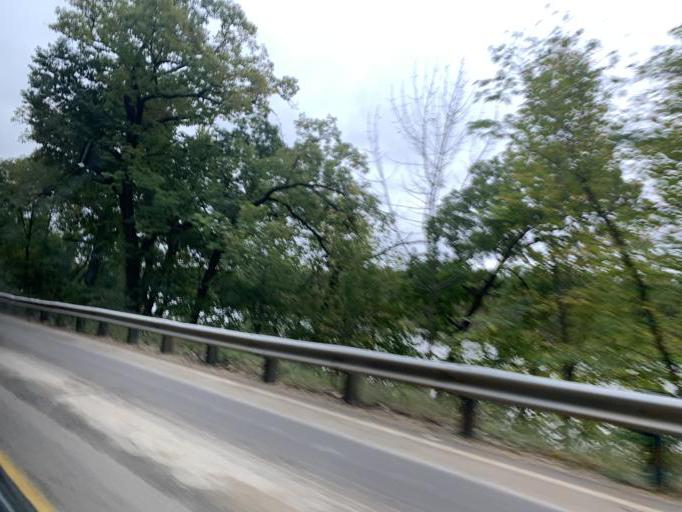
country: US
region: Wisconsin
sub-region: Grant County
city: Muscoda
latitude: 43.2077
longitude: -90.3710
